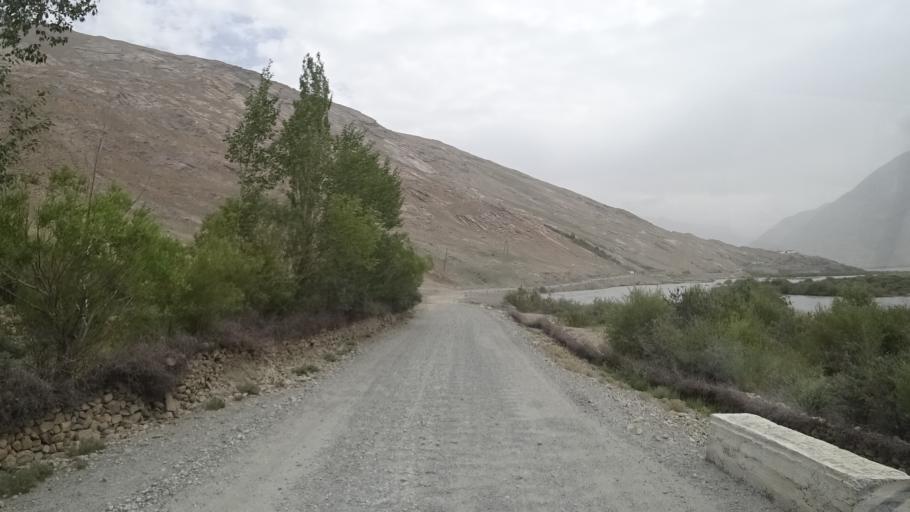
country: AF
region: Badakhshan
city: Khandud
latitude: 37.0041
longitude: 72.5328
